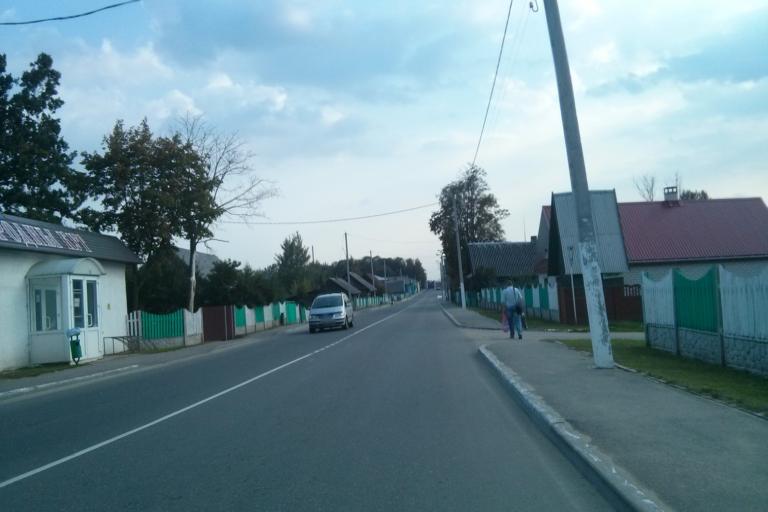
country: BY
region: Minsk
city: Chervyen'
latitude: 53.7183
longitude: 28.4180
